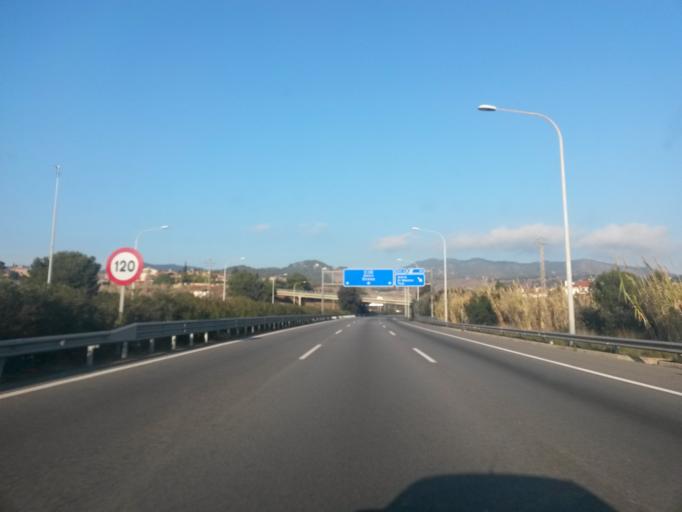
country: ES
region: Catalonia
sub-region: Provincia de Barcelona
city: Alella
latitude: 41.4844
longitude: 2.2958
